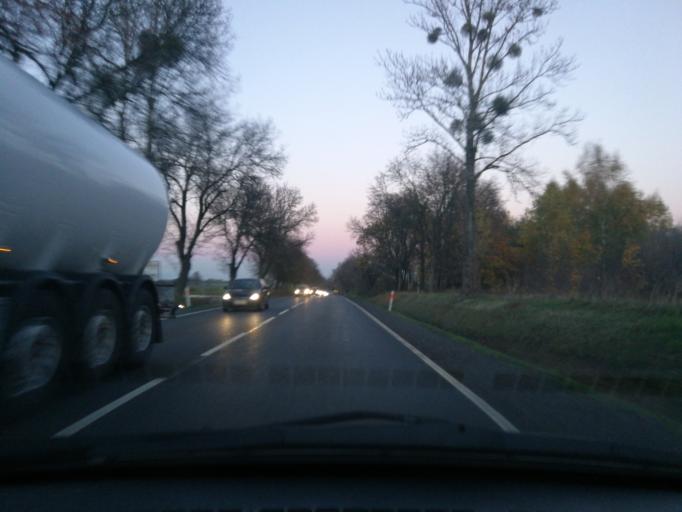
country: PL
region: Lodz Voivodeship
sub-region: Powiat lodzki wschodni
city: Andrespol
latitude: 51.8030
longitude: 19.6488
